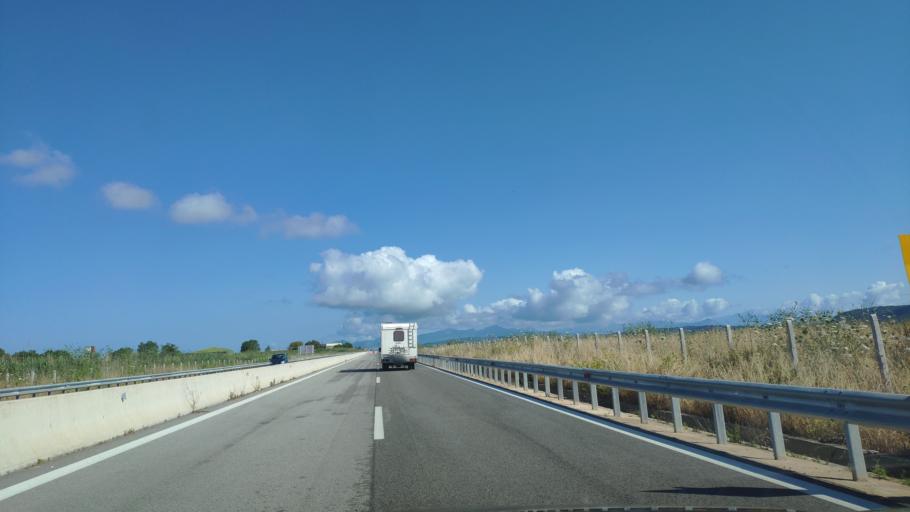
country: GR
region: Epirus
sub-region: Nomos Prevezis
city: Preveza
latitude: 38.9224
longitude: 20.7876
